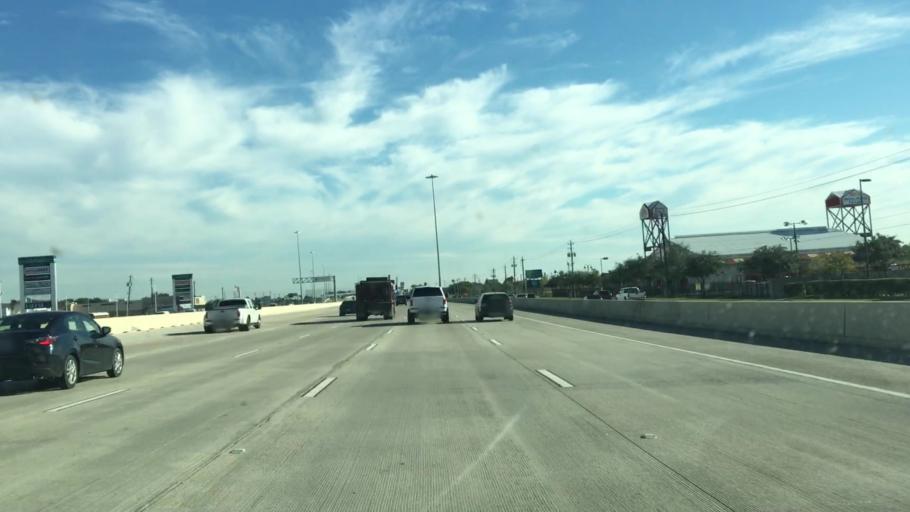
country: US
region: Texas
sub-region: Harris County
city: Webster
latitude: 29.5376
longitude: -95.1395
